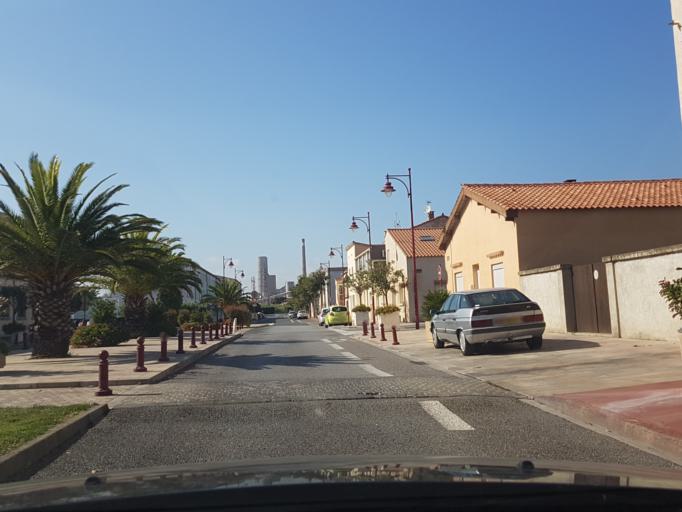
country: FR
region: Languedoc-Roussillon
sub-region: Departement de l'Aude
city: Port-la-Nouvelle
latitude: 43.0203
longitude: 3.0427
